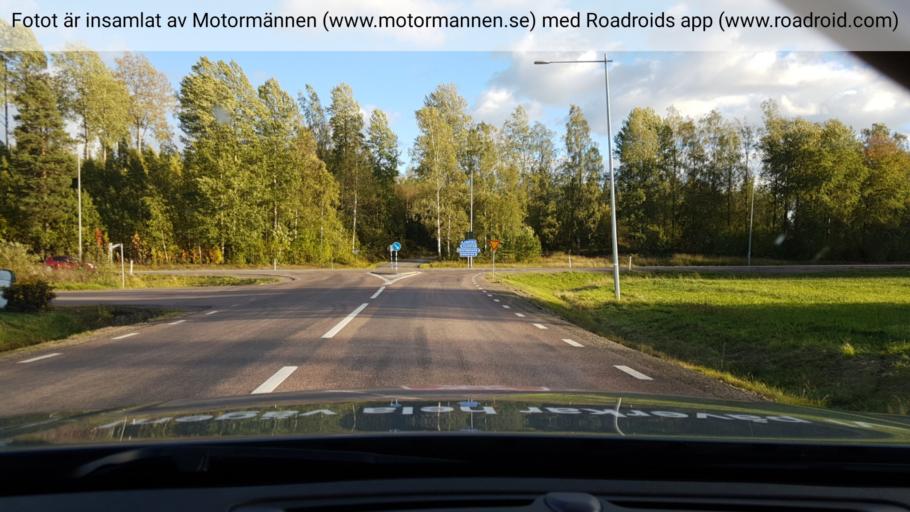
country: SE
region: Vaermland
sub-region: Karlstads Kommun
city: Molkom
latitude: 59.6042
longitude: 13.7394
